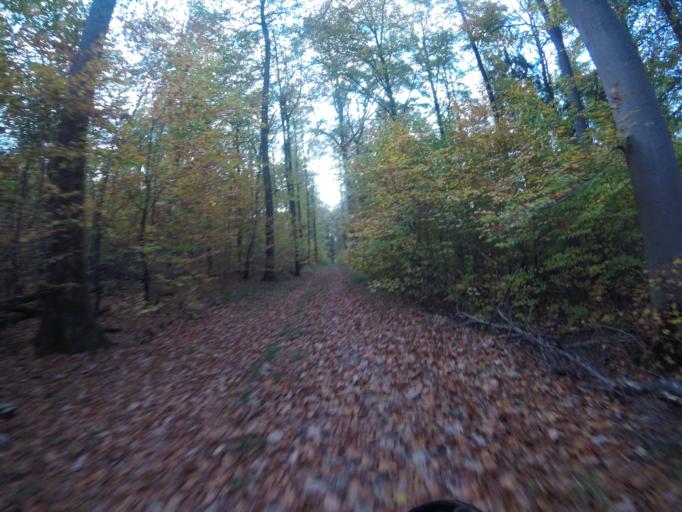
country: DE
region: Baden-Wuerttemberg
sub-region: Regierungsbezirk Stuttgart
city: Kirchberg an der Murr
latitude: 48.9807
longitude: 9.3580
